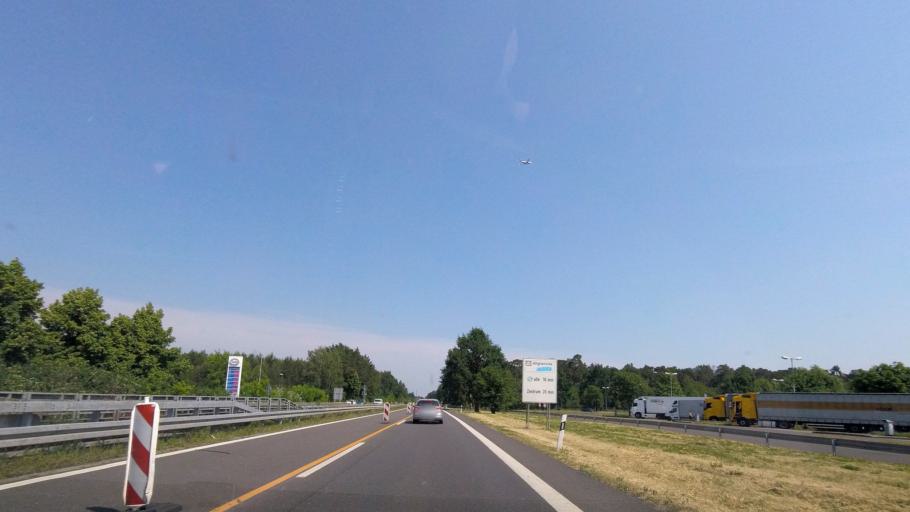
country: DE
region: Berlin
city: Bohnsdorf
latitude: 52.3781
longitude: 13.5623
